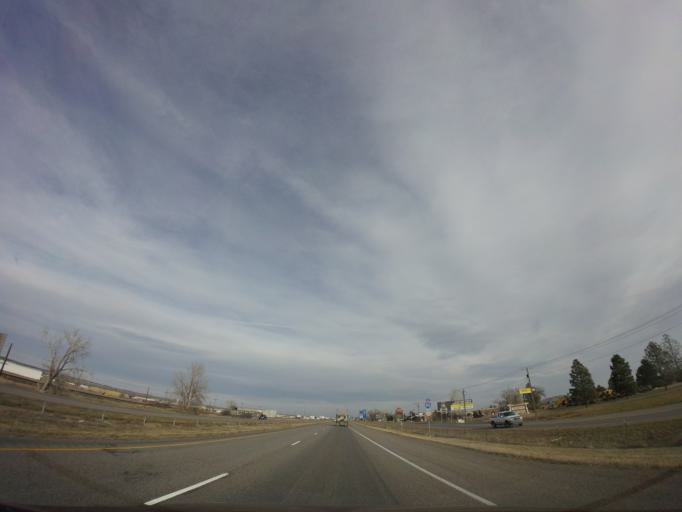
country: US
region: Montana
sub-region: Yellowstone County
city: Billings
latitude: 45.7371
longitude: -108.5938
